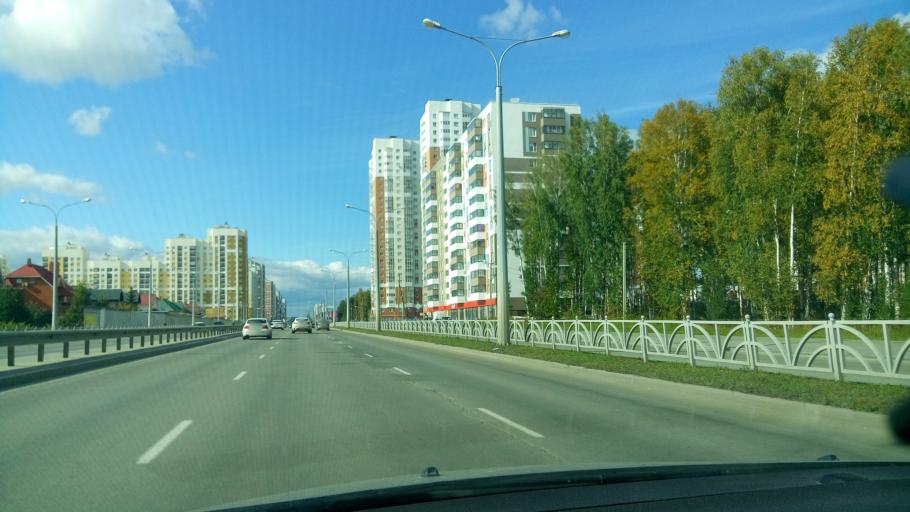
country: RU
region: Sverdlovsk
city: Sovkhoznyy
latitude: 56.7857
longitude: 60.5350
